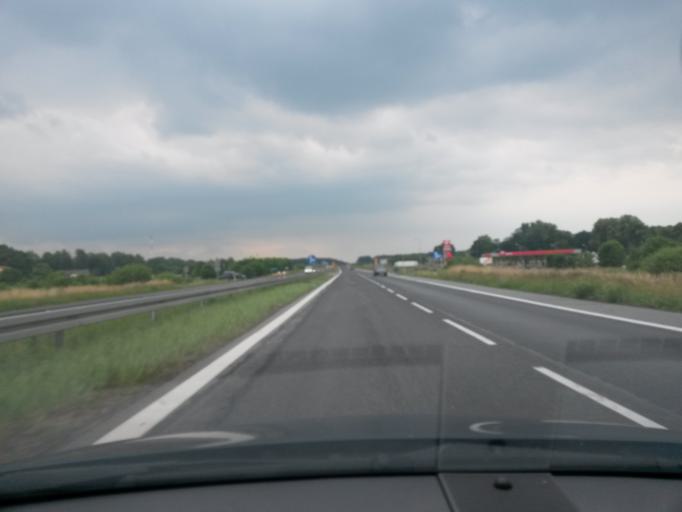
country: PL
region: Silesian Voivodeship
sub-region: Powiat czestochowski
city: Borowno
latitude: 50.9980
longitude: 19.2917
